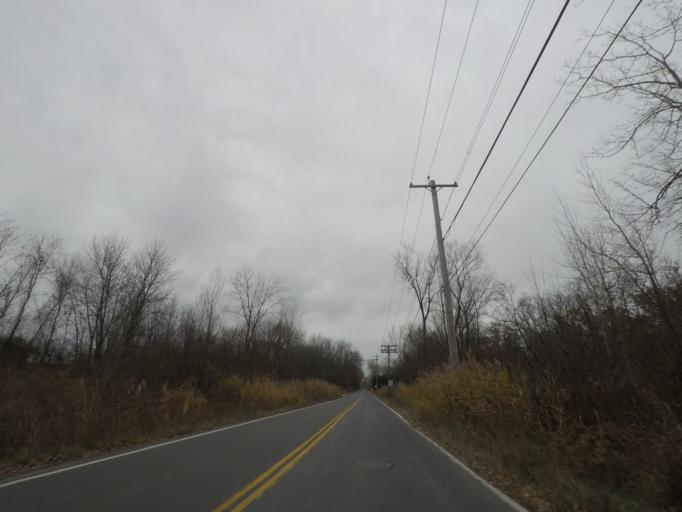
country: US
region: New York
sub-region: Albany County
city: Cohoes
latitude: 42.7971
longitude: -73.7300
